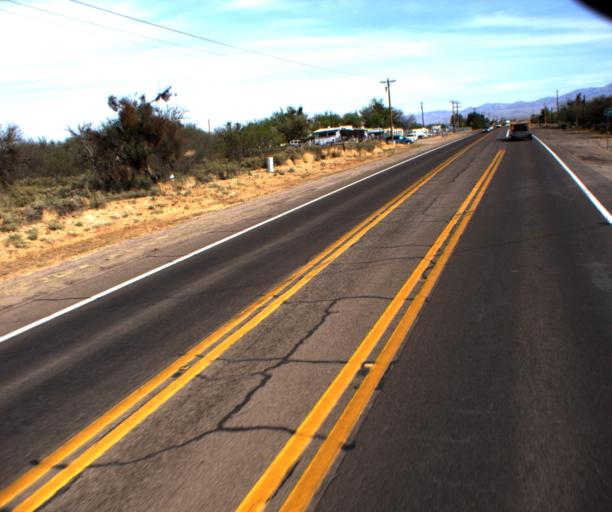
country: US
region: Arizona
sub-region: Graham County
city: Cactus Flat
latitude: 32.7645
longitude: -109.7163
